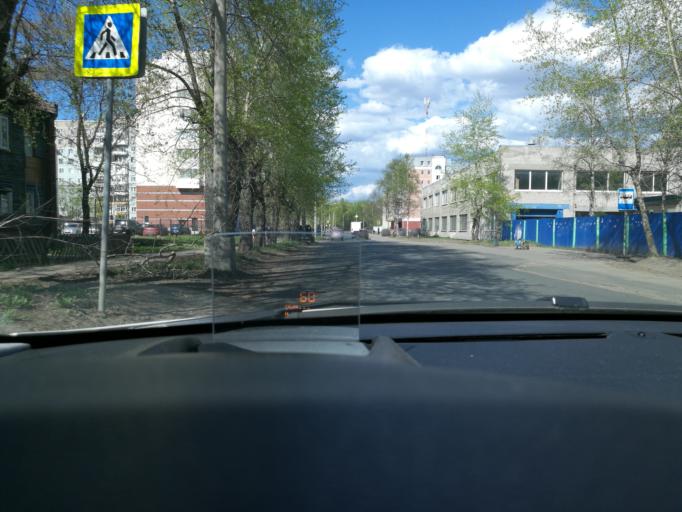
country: RU
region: Arkhangelskaya
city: Arkhangel'sk
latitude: 64.5531
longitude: 40.5375
